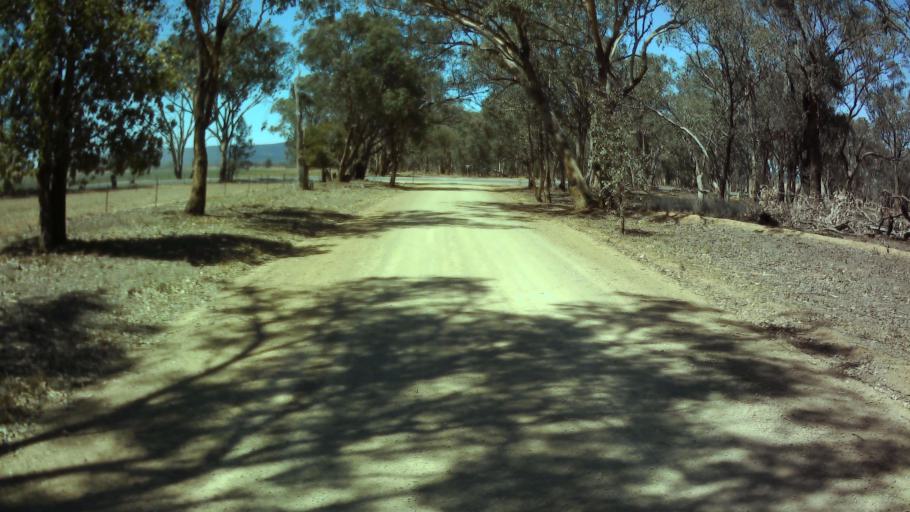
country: AU
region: New South Wales
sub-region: Weddin
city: Grenfell
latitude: -33.9064
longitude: 148.0807
